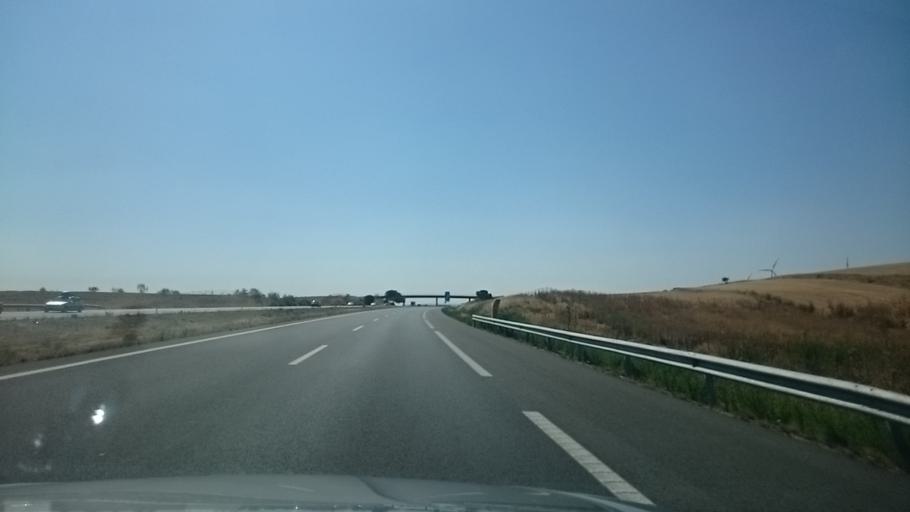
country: ES
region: Aragon
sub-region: Provincia de Zaragoza
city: Luceni
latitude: 41.8118
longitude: -1.2700
